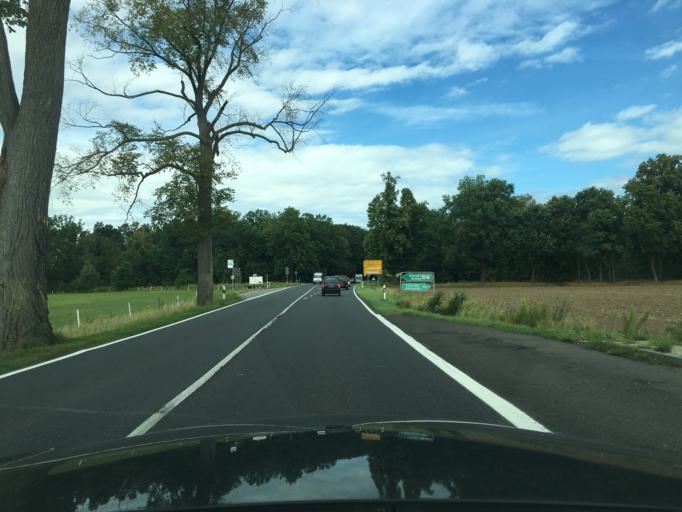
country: DE
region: Brandenburg
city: Gransee
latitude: 52.9646
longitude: 13.1489
